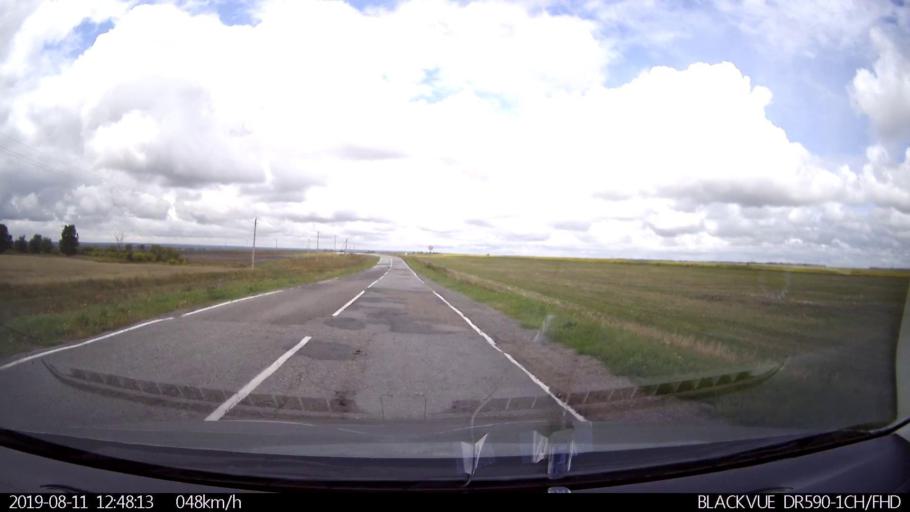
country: RU
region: Ulyanovsk
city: Ignatovka
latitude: 53.8729
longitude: 47.7012
